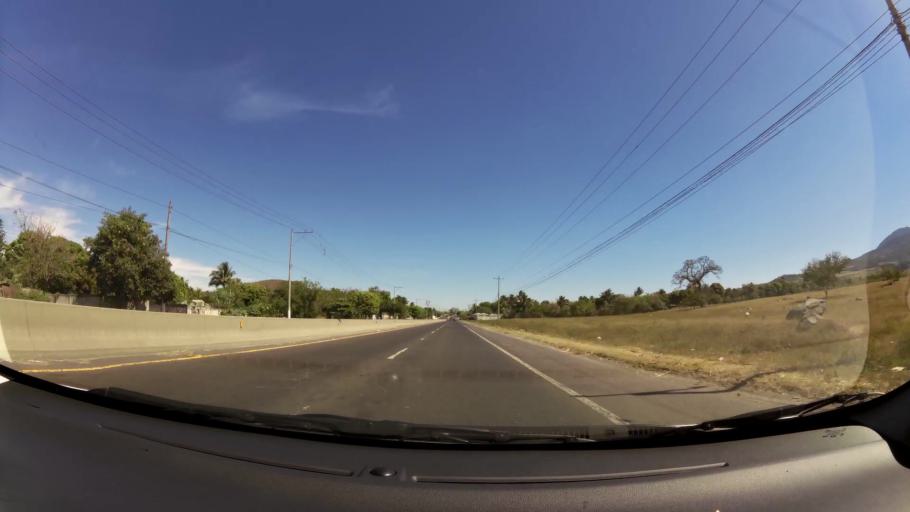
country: SV
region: La Libertad
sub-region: Distrito de Quezaltepeque
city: Quezaltepeque
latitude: 13.7956
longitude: -89.3452
